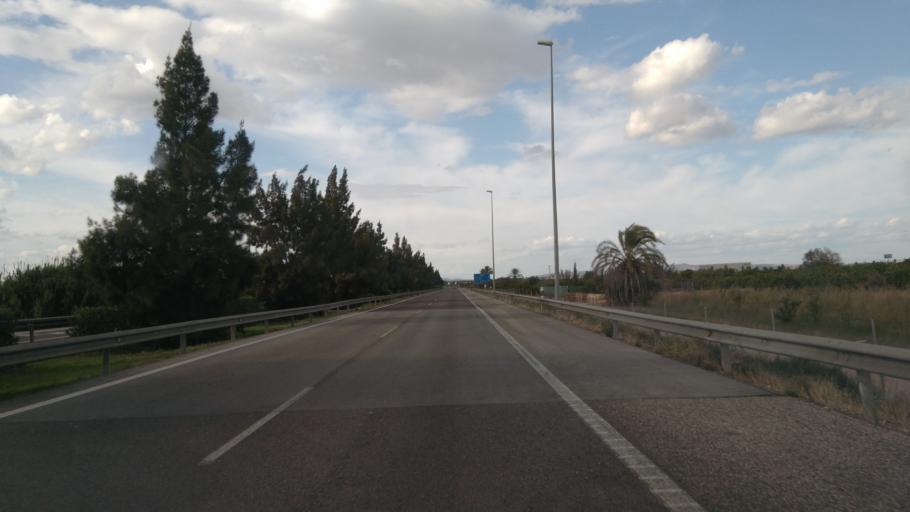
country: ES
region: Valencia
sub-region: Provincia de Valencia
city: Guadassuar
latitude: 39.1648
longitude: -0.4584
